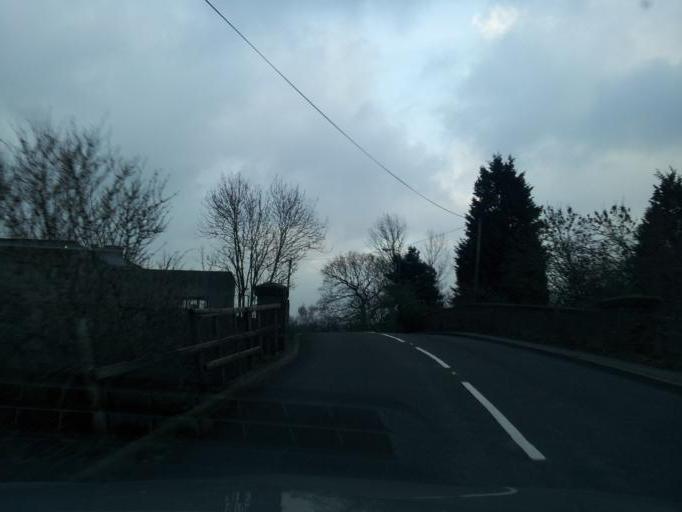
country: GB
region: England
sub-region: Derbyshire
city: Etwall
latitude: 52.8639
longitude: -1.6154
